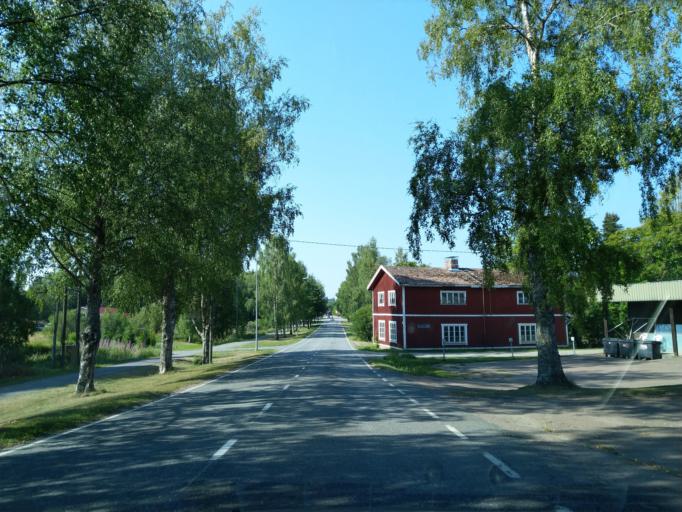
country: FI
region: Satakunta
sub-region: Pori
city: Pomarkku
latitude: 61.7003
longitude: 22.0174
